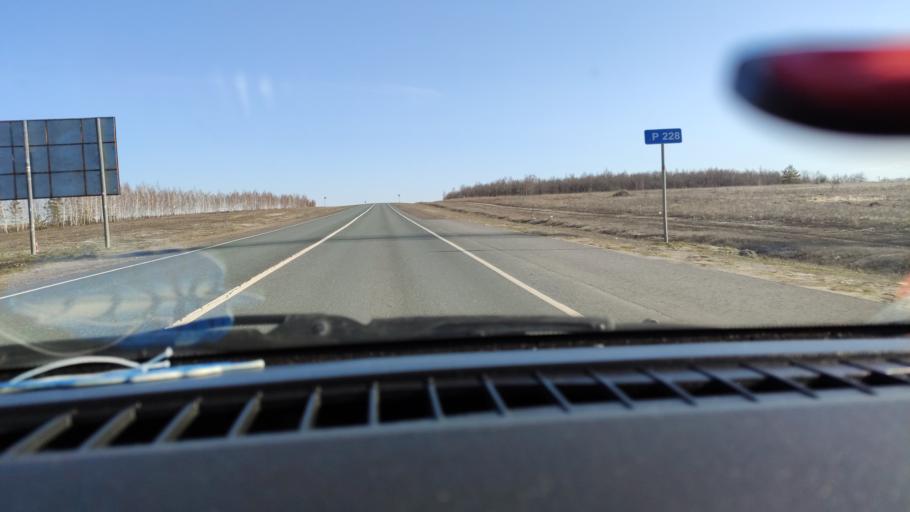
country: RU
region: Samara
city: Syzran'
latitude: 52.9289
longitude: 48.3056
